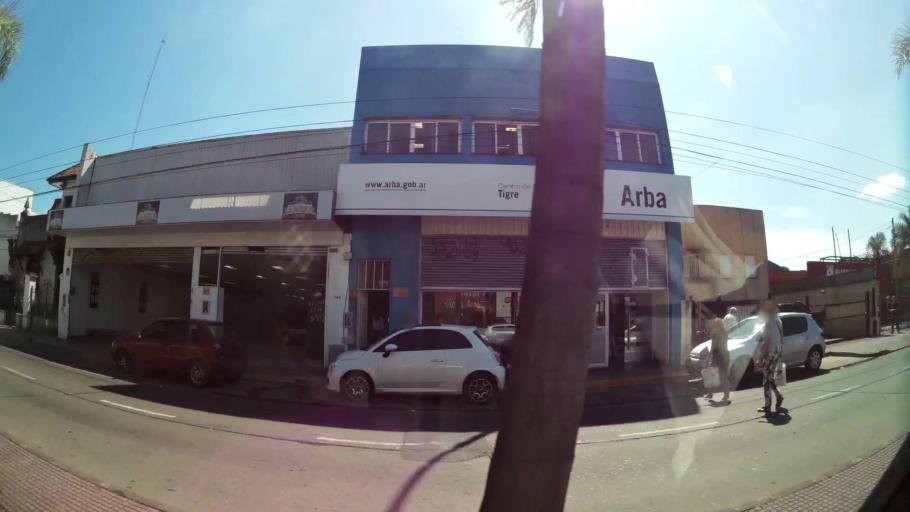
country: AR
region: Buenos Aires
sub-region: Partido de Tigre
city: Tigre
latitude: -34.4295
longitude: -58.5722
